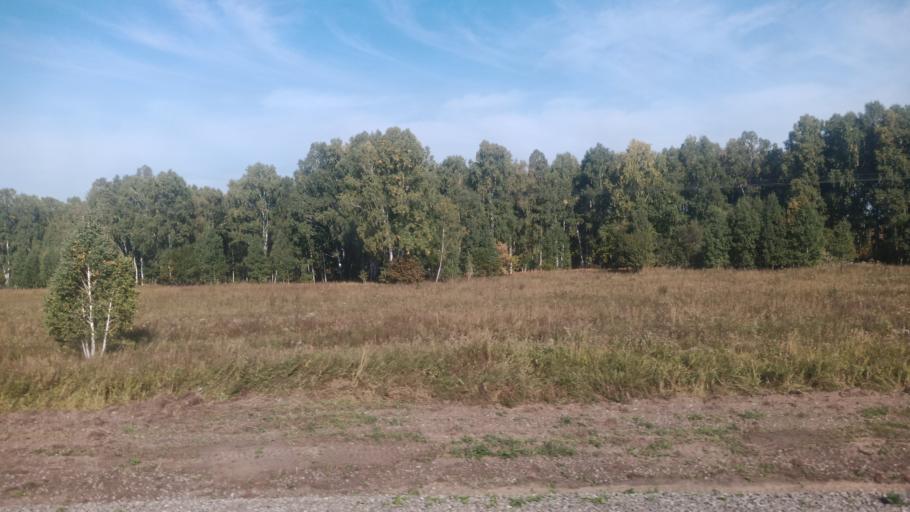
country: RU
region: Altai Krai
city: Troitskoye
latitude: 53.0951
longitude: 84.6693
